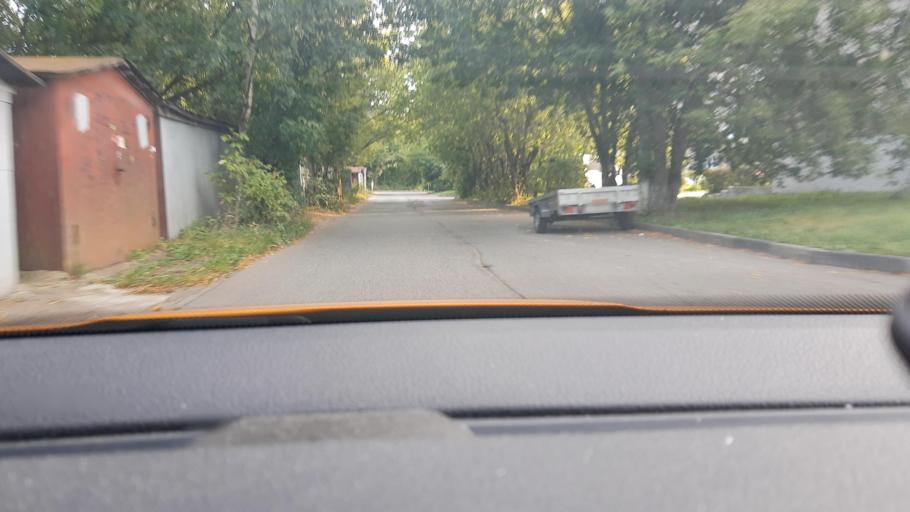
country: RU
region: Moskovskaya
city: Bolshevo
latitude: 55.9514
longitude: 37.8363
